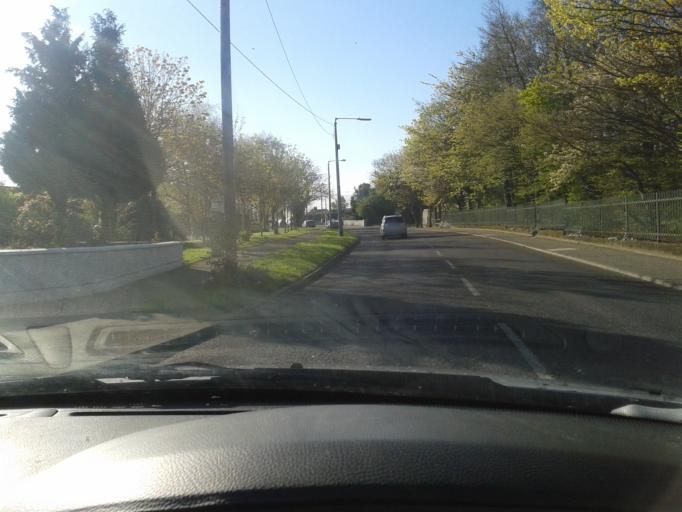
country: IE
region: Leinster
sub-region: Fingal County
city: Swords
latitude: 53.4635
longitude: -6.2339
